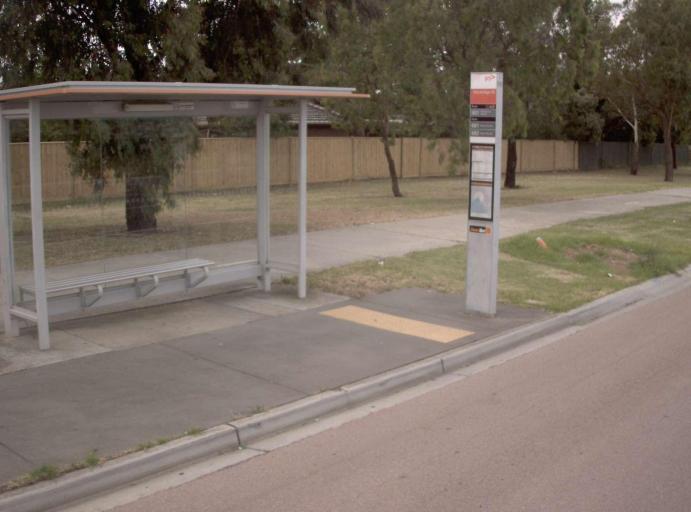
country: AU
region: Victoria
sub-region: Knox
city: Scoresby
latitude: -37.8855
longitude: 145.2329
